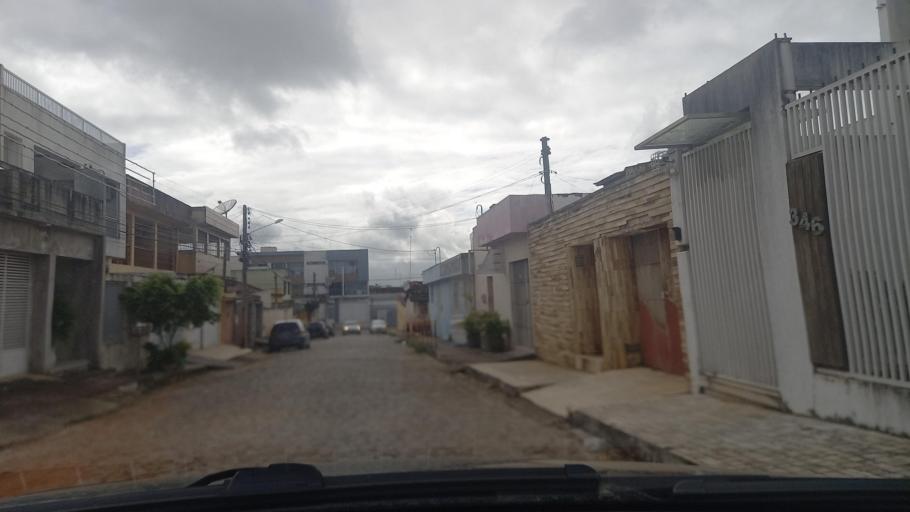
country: BR
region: Pernambuco
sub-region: Vitoria De Santo Antao
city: Vitoria de Santo Antao
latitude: -8.1106
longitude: -35.2989
